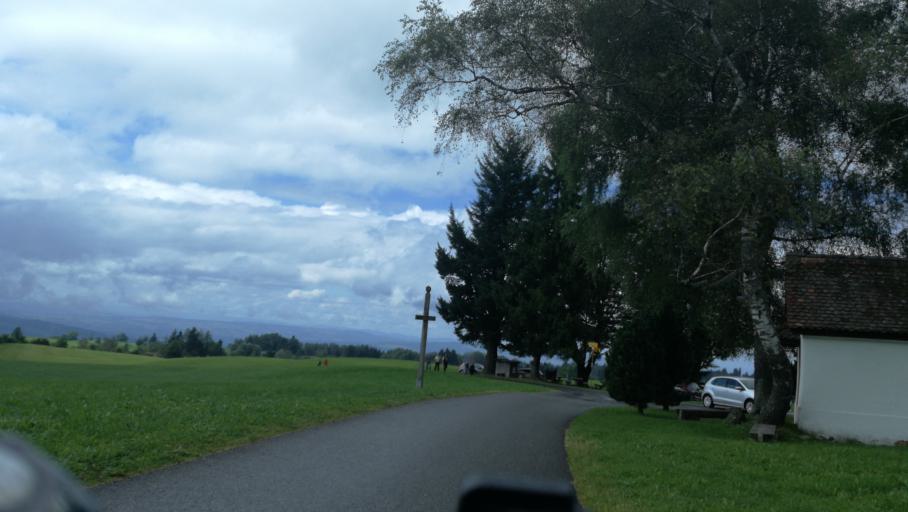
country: CH
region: Zug
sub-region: Zug
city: Walchwil
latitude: 47.1117
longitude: 8.5440
